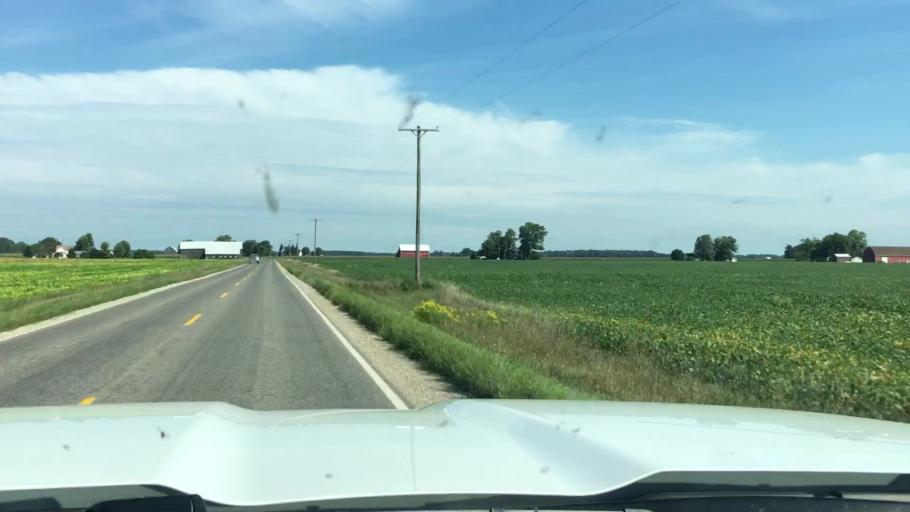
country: US
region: Michigan
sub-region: Saginaw County
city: Hemlock
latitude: 43.5054
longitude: -84.2297
